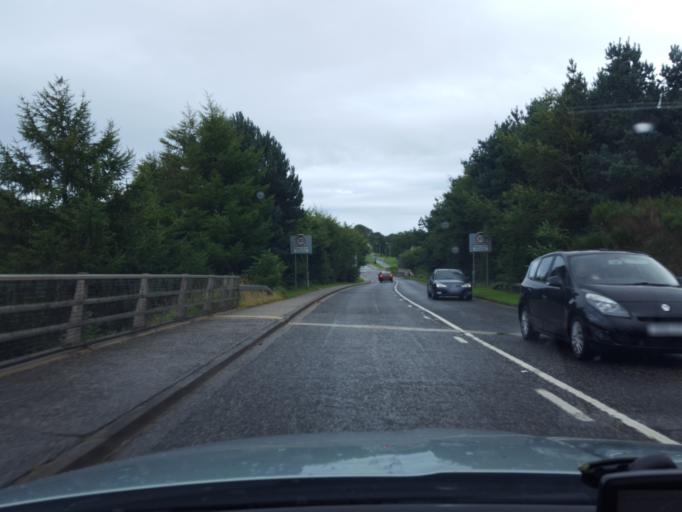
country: GB
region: Scotland
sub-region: Aberdeenshire
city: Stonehaven
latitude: 56.9743
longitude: -2.2327
